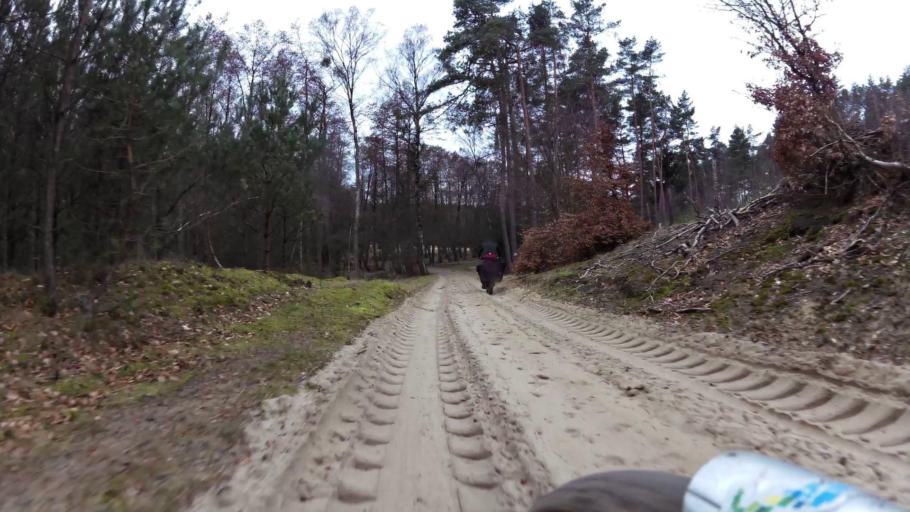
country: PL
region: Pomeranian Voivodeship
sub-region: Powiat bytowski
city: Trzebielino
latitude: 54.1291
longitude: 17.1361
